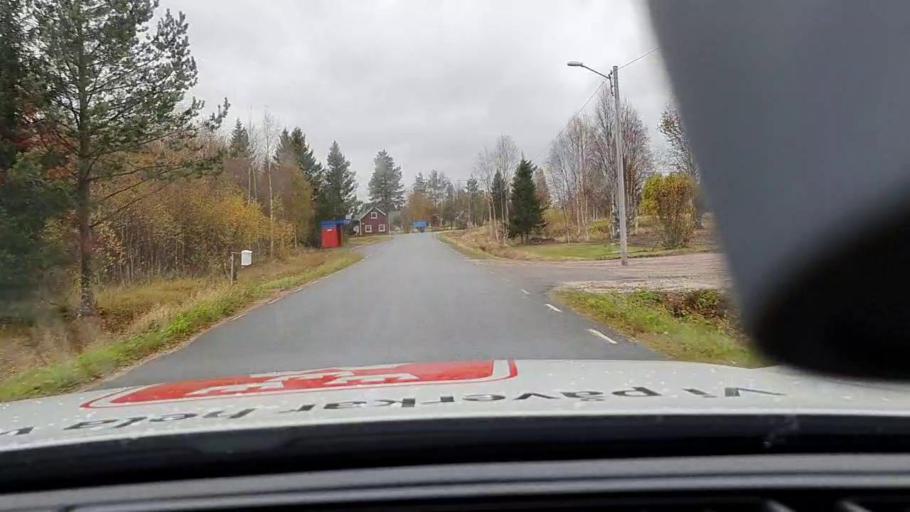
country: SE
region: Norrbotten
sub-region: Haparanda Kommun
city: Haparanda
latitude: 65.9467
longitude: 23.7988
